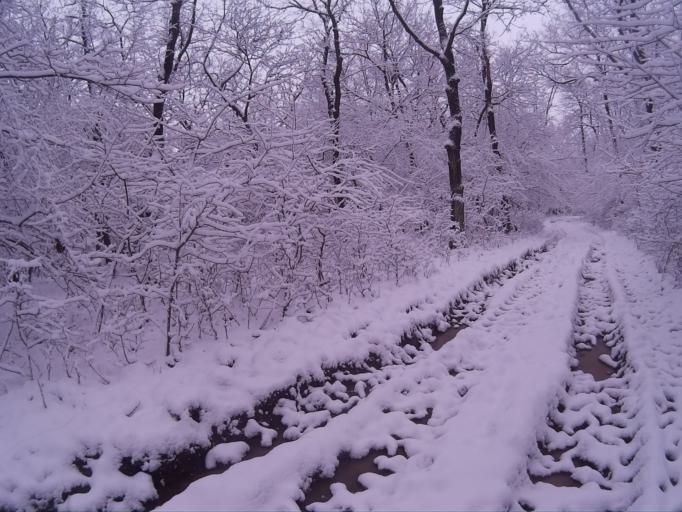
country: HU
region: Komarom-Esztergom
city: Tarjan
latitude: 47.5690
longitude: 18.5370
